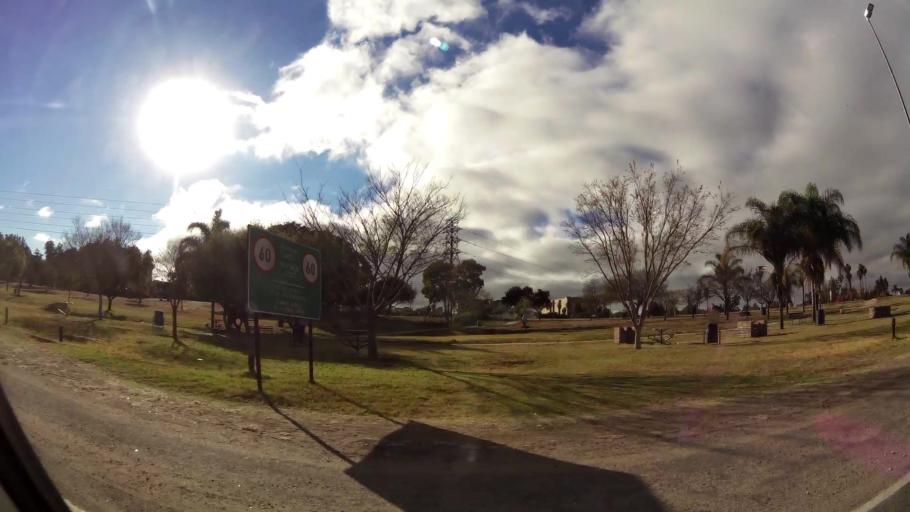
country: ZA
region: Limpopo
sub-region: Capricorn District Municipality
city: Polokwane
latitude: -23.9128
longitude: 29.4447
